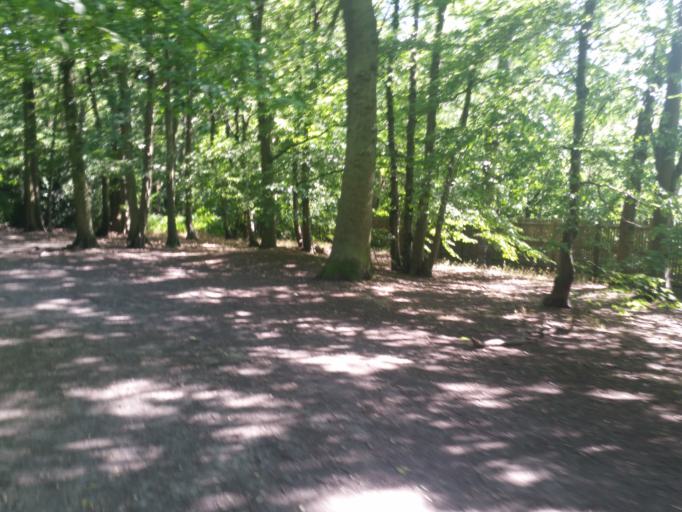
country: GB
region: England
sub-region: Greater London
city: Crouch End
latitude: 51.5828
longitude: -0.1533
